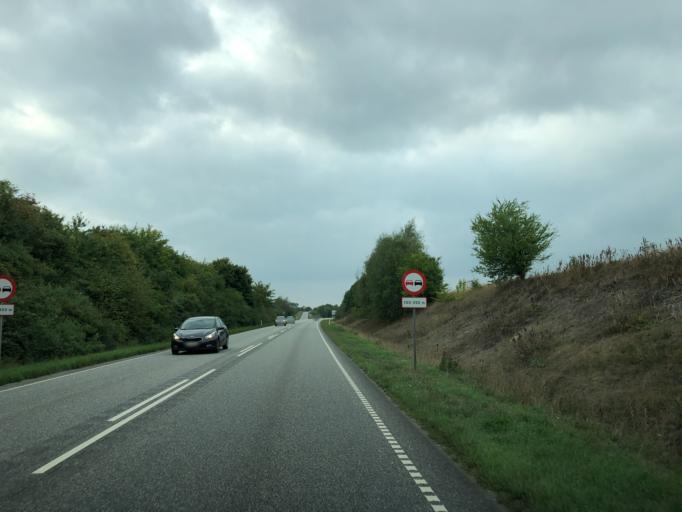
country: DK
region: South Denmark
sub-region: Vejle Kommune
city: Brejning
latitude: 55.6308
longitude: 9.6946
